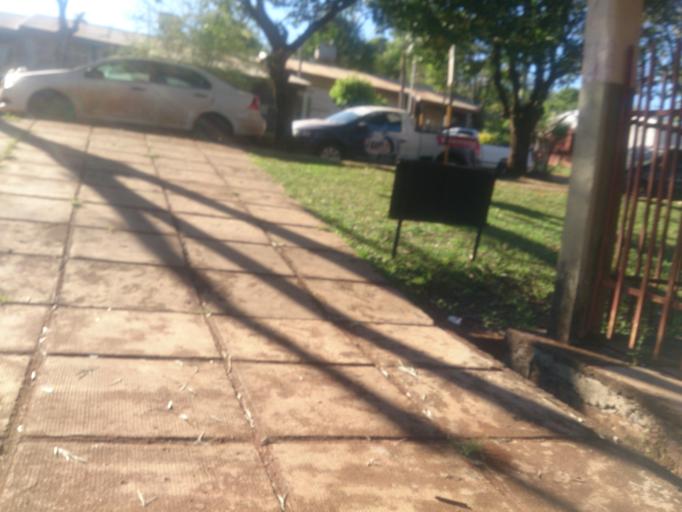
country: AR
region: Misiones
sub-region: Departamento de Obera
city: Obera
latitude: -27.4883
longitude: -55.1011
